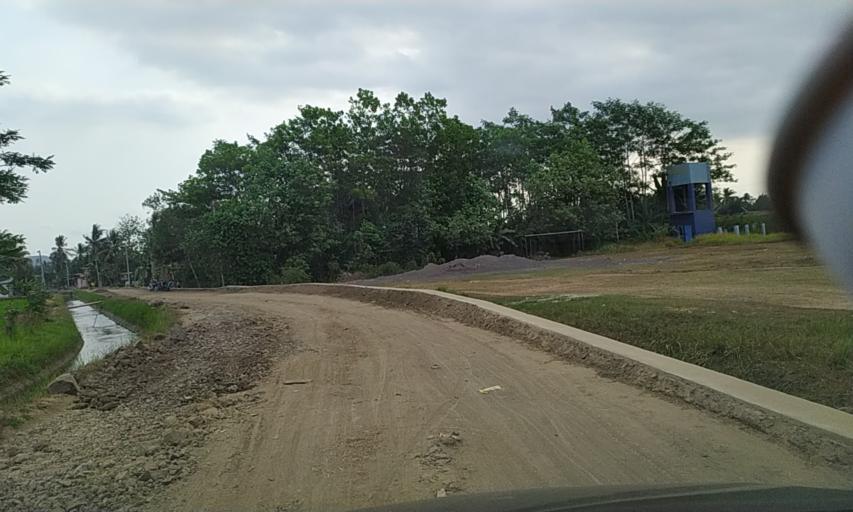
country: ID
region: Central Java
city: Mulyadadi
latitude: -7.3254
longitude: 108.7605
